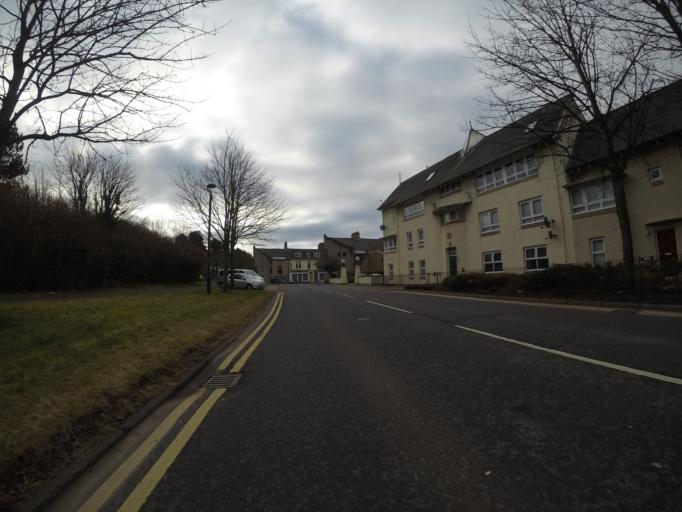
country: GB
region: Scotland
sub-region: North Ayrshire
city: Irvine
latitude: 55.6119
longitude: -4.6760
